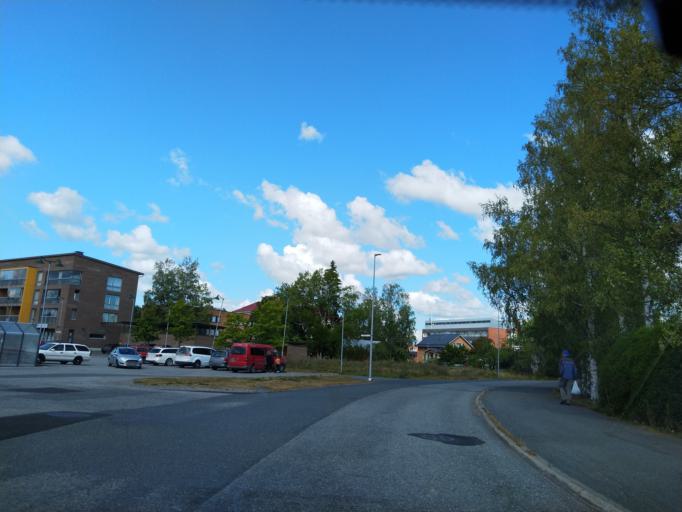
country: FI
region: Satakunta
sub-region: Pori
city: Huittinen
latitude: 61.1787
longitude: 22.6992
